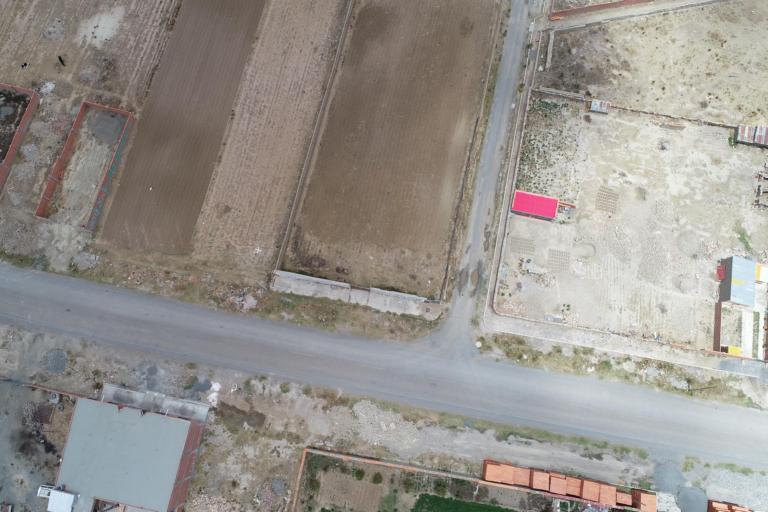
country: BO
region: La Paz
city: Achacachi
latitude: -16.0459
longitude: -68.6922
